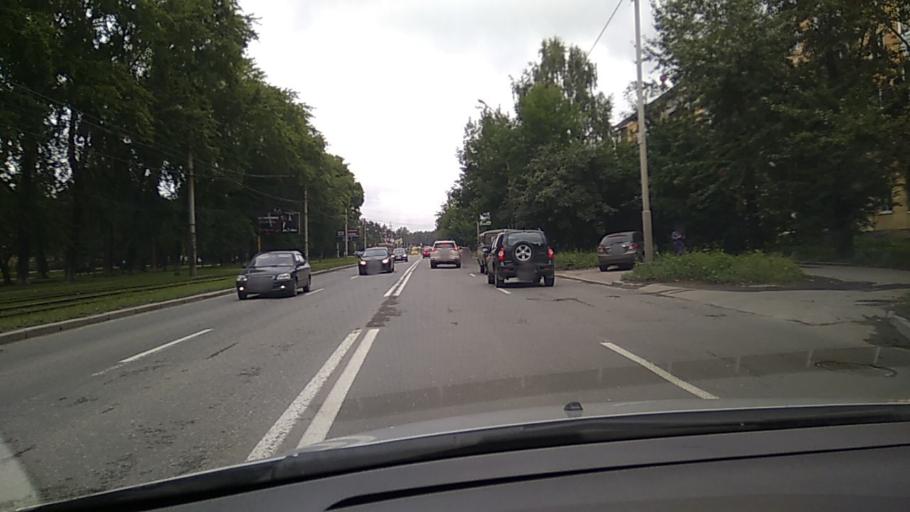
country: RU
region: Sverdlovsk
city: Sovkhoznyy
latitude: 56.7774
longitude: 60.6117
